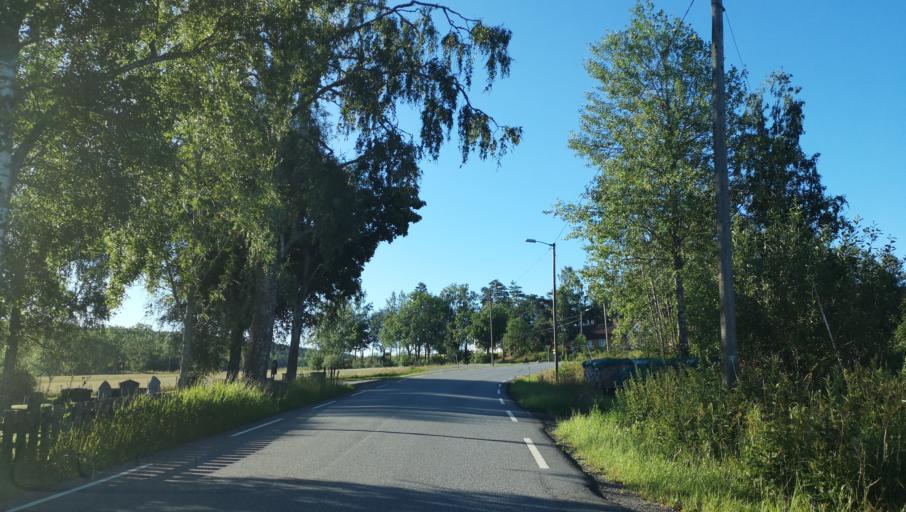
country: NO
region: Ostfold
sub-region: Hobol
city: Tomter
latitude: 59.6532
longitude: 11.0097
